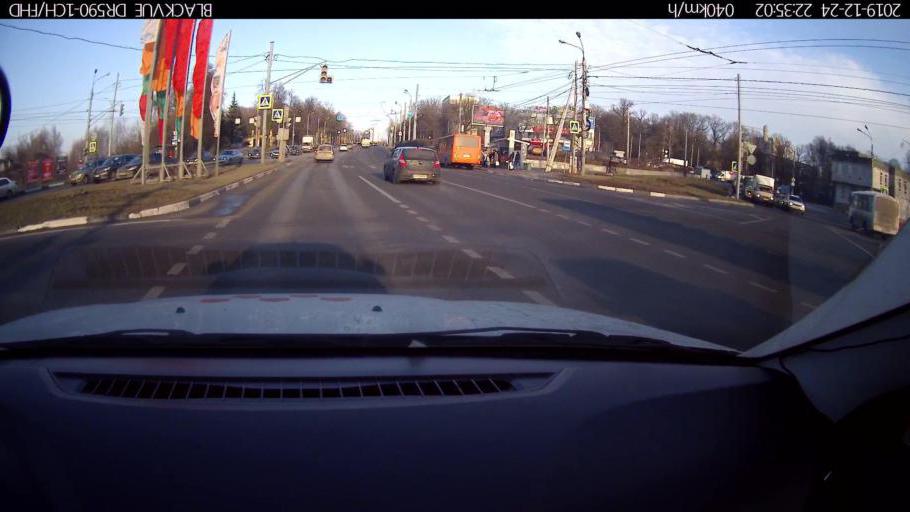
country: RU
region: Nizjnij Novgorod
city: Nizhniy Novgorod
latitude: 56.2554
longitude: 43.9694
